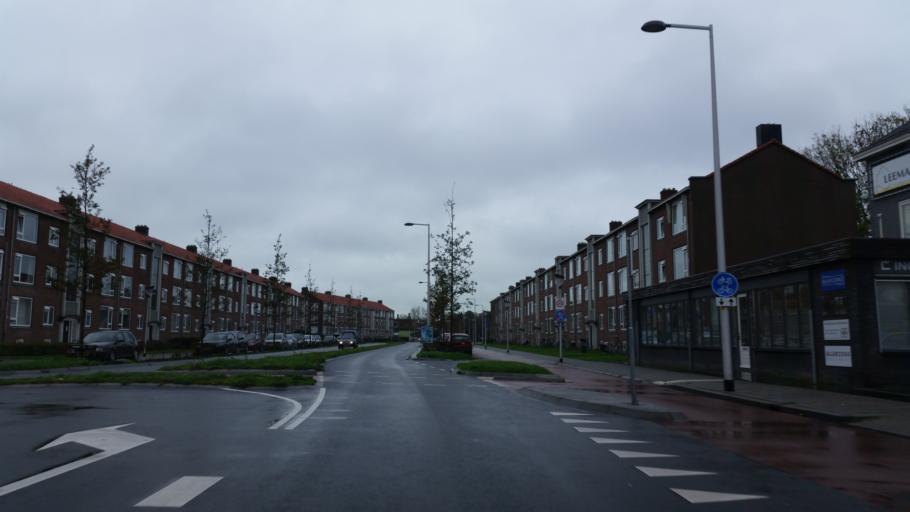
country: NL
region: Friesland
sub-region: Gemeente Leeuwarden
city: Bilgaard
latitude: 53.2086
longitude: 5.7785
